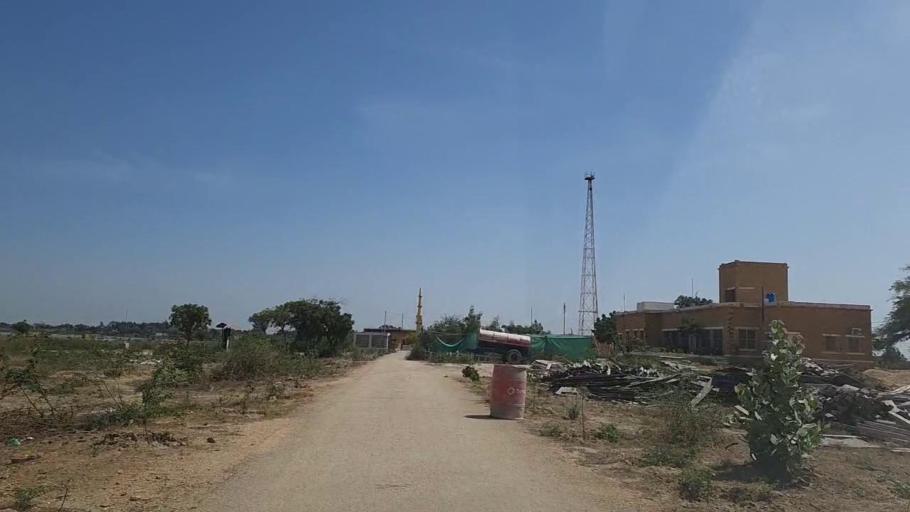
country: PK
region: Sindh
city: Gharo
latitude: 24.7914
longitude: 67.7486
